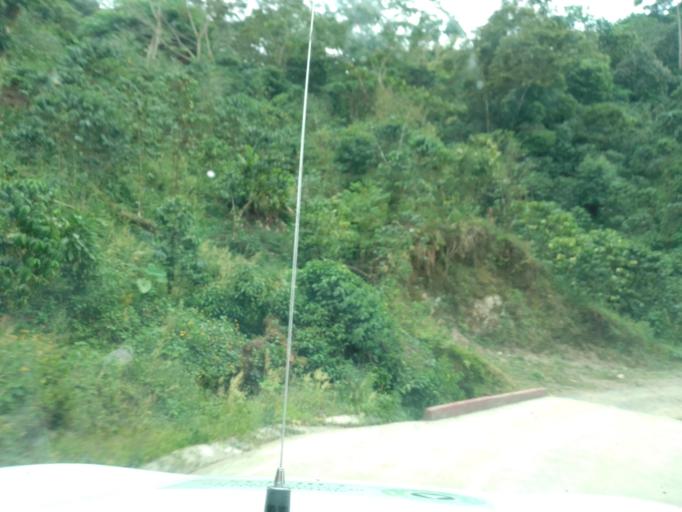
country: MX
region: Chiapas
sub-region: Union Juarez
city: Santo Domingo
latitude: 15.0668
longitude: -92.1162
